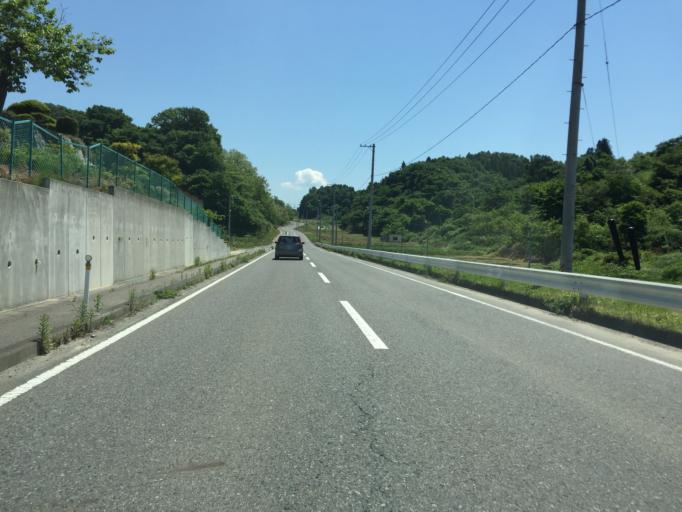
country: JP
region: Fukushima
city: Motomiya
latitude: 37.5238
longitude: 140.4491
